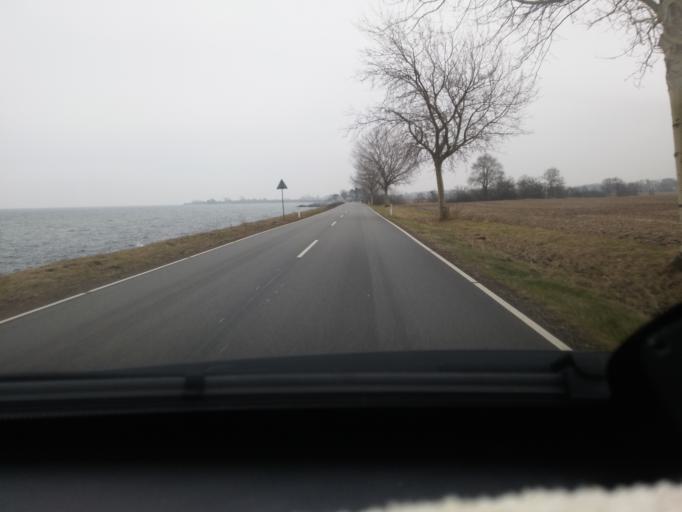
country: DK
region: South Denmark
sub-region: Kerteminde Kommune
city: Kerteminde
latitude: 55.4272
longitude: 10.6975
